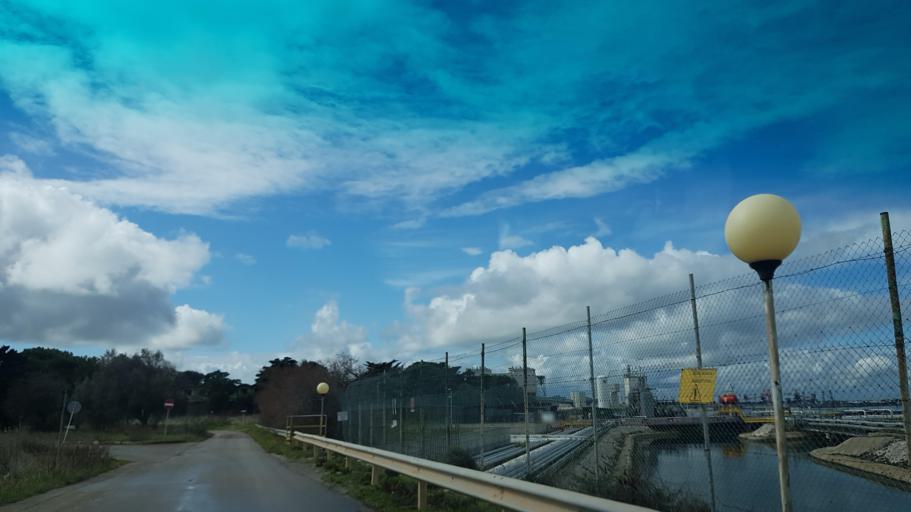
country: IT
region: Apulia
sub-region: Provincia di Brindisi
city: Materdomini
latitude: 40.6457
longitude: 17.9911
